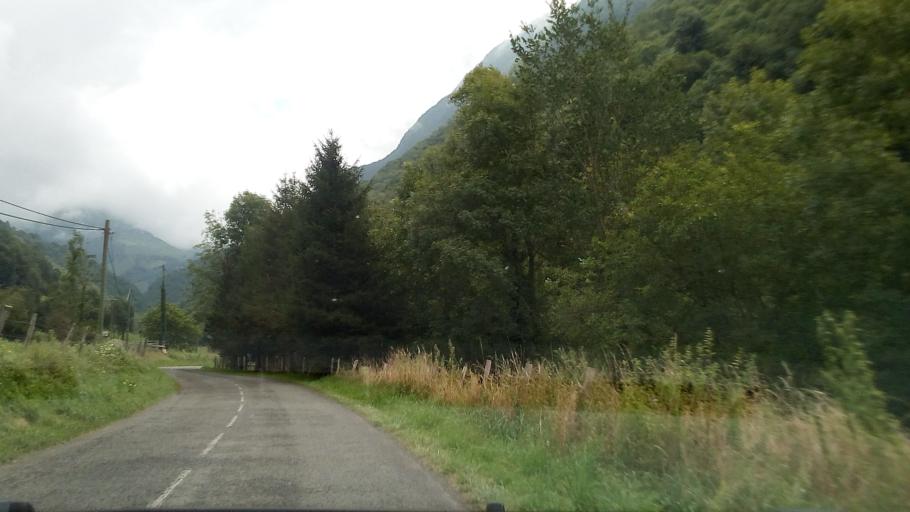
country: FR
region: Aquitaine
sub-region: Departement des Pyrenees-Atlantiques
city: Arette
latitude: 43.0769
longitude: -0.6042
